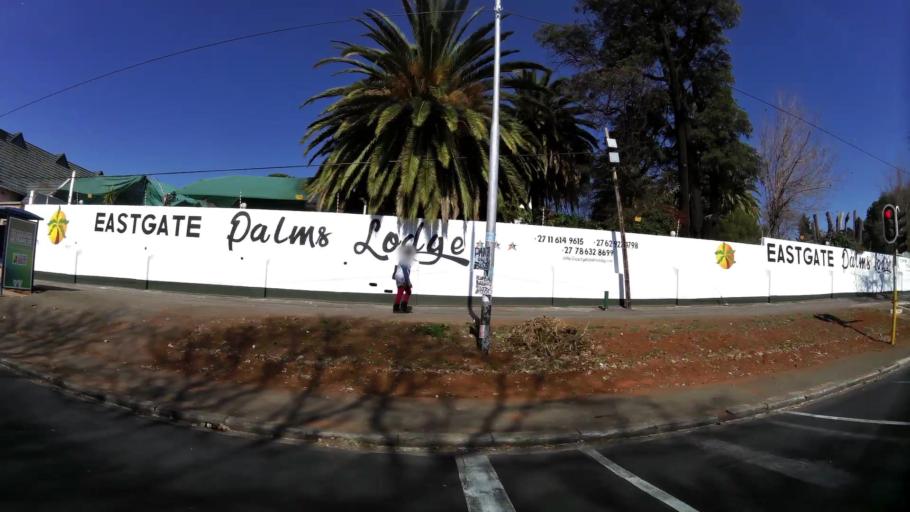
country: ZA
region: Gauteng
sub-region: City of Johannesburg Metropolitan Municipality
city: Johannesburg
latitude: -26.1944
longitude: 28.0766
